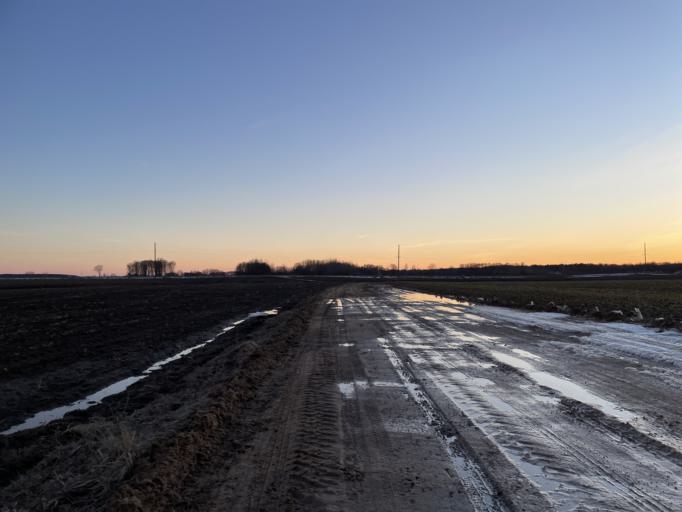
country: BY
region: Minsk
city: Nyasvizh
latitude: 53.2061
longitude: 26.6771
